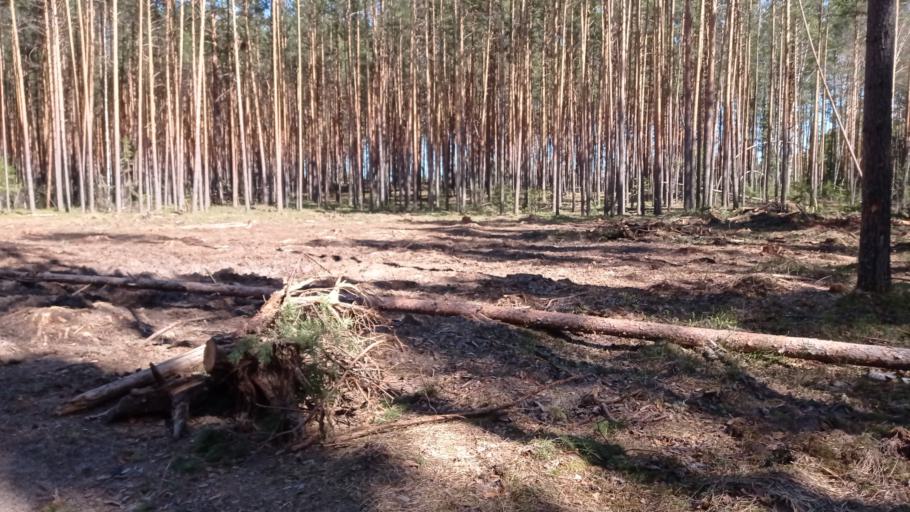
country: RU
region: Tomsk
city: Timiryazevskoye
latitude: 56.4265
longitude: 84.7615
